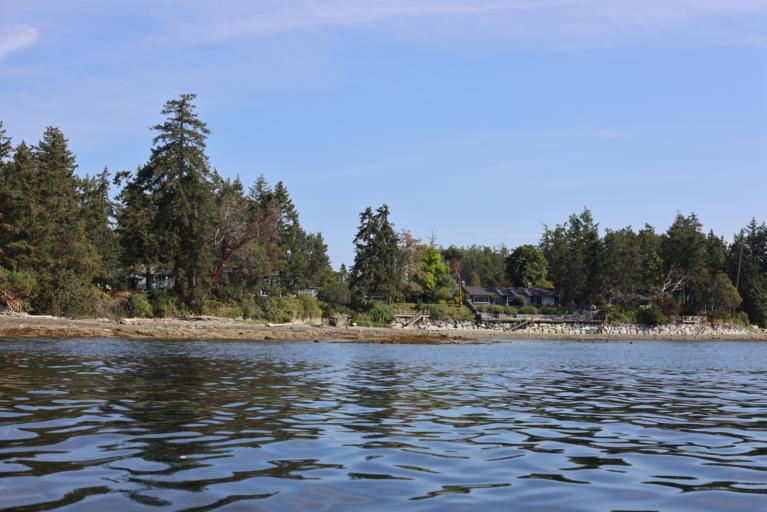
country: CA
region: British Columbia
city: North Saanich
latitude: 48.6630
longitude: -123.4700
